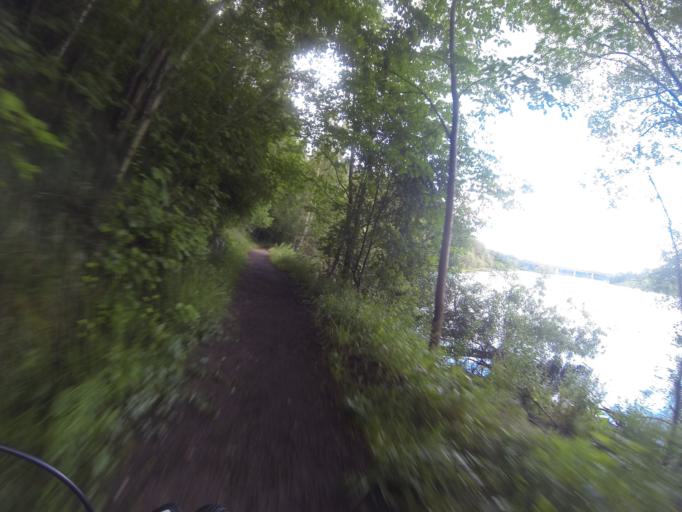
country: SE
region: Dalarna
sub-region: Avesta Kommun
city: Avesta
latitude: 60.1503
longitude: 16.1855
